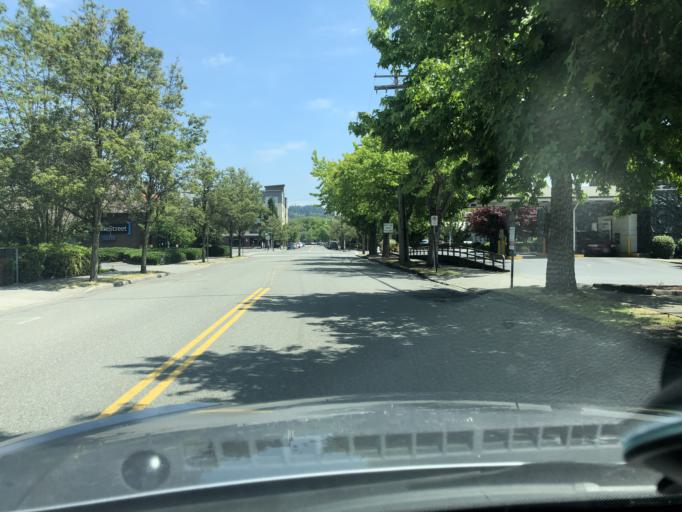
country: US
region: Washington
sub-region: King County
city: Kent
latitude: 47.3821
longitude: -122.2385
